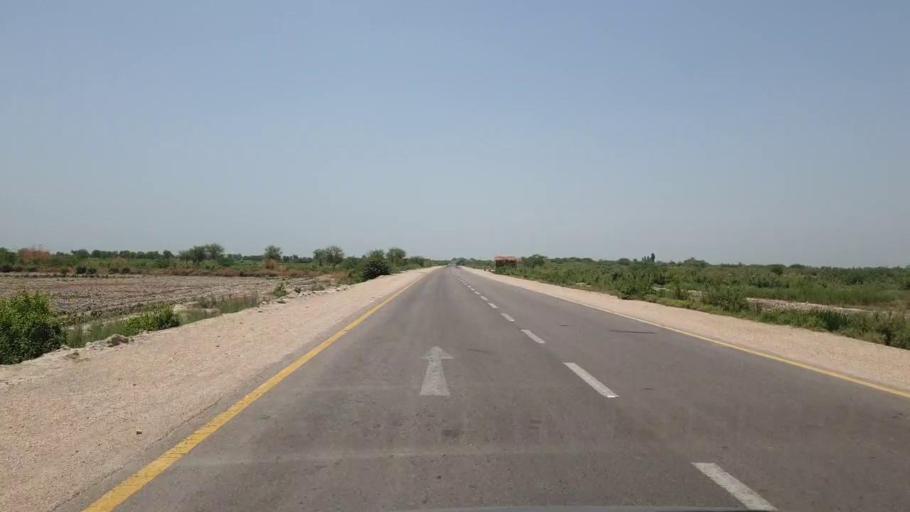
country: PK
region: Sindh
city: Sakrand
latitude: 26.1202
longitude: 68.3843
